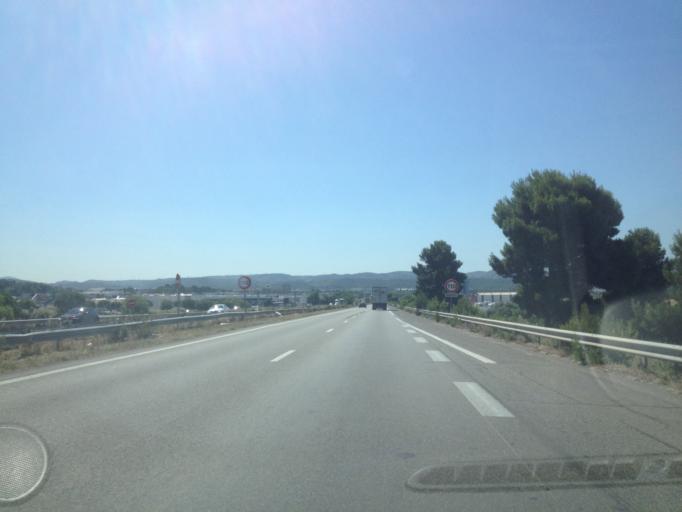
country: FR
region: Provence-Alpes-Cote d'Azur
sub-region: Departement des Bouches-du-Rhone
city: Vitrolles
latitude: 43.4361
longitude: 5.2535
